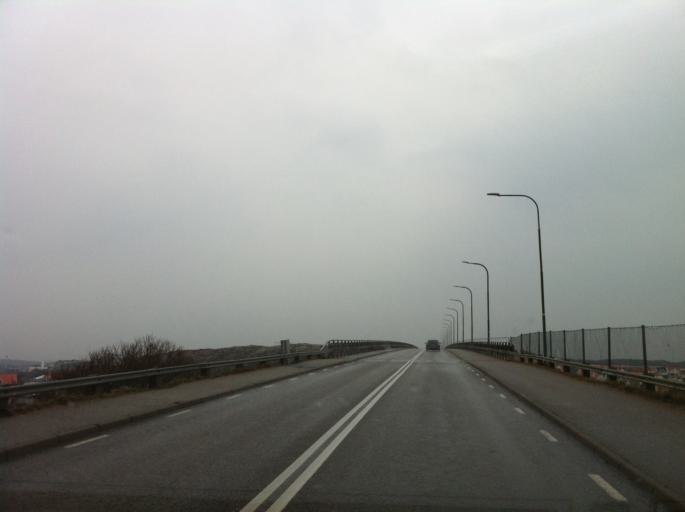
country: SE
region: Vaestra Goetaland
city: Smoegen
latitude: 58.3638
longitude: 11.2384
